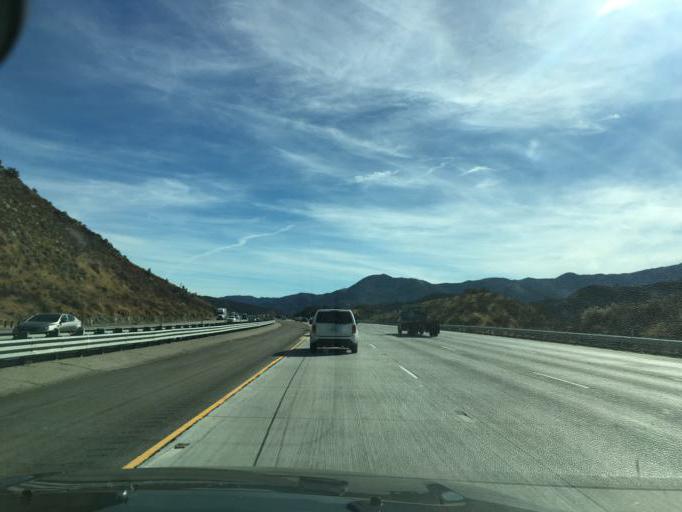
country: US
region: California
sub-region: Kern County
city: Lebec
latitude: 34.6994
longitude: -118.7928
